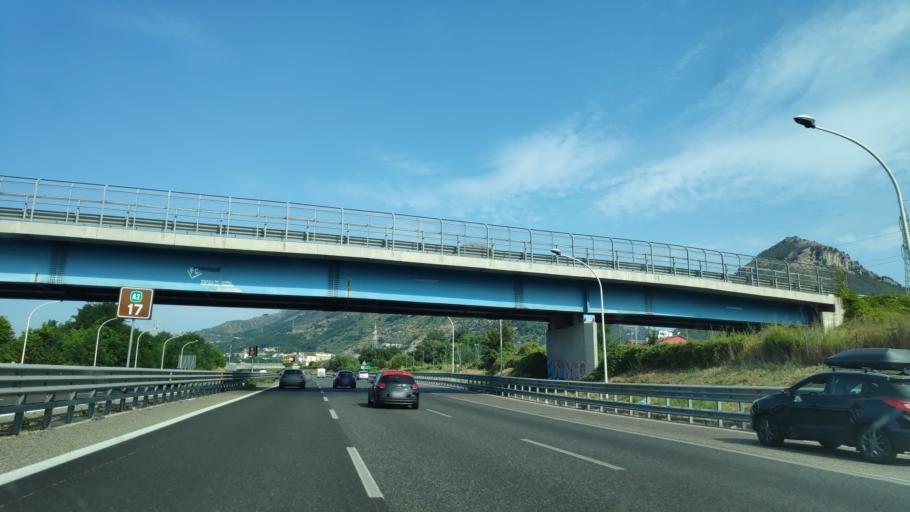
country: IT
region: Campania
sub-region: Provincia di Salerno
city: San Mango Piemonte
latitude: 40.6935
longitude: 14.8336
